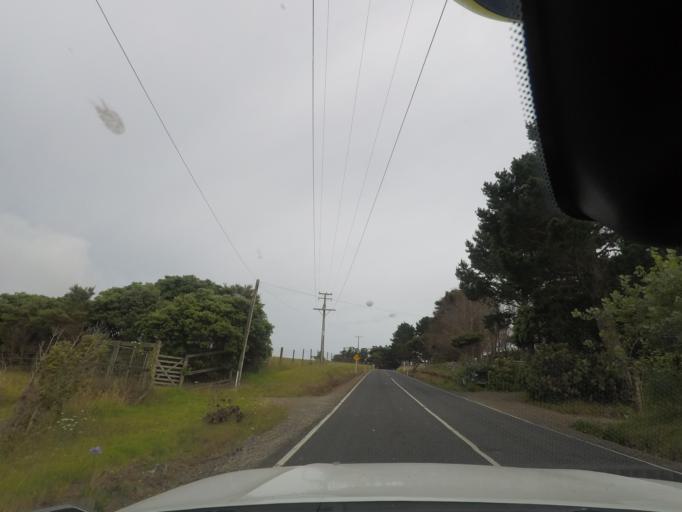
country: NZ
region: Auckland
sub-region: Auckland
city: Parakai
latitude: -36.4990
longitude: 174.2483
